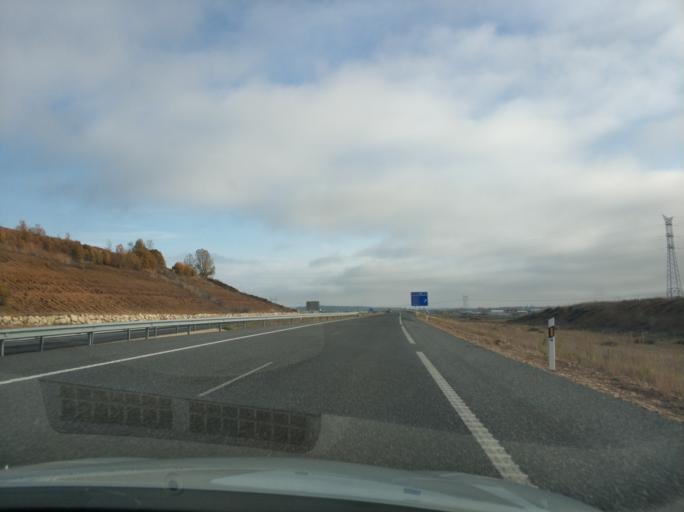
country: ES
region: Castille and Leon
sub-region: Provincia de Leon
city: Valdefresno
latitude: 42.5607
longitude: -5.4756
